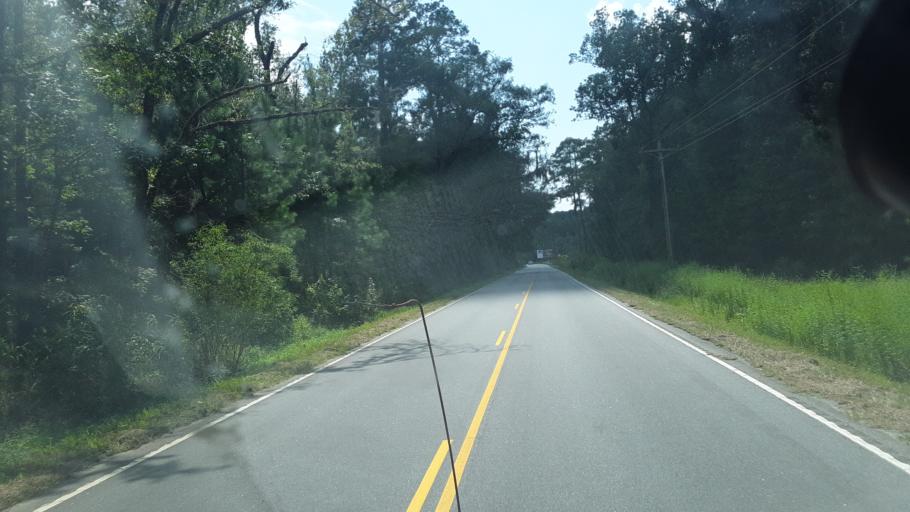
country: US
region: South Carolina
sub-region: Jasper County
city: Ridgeland
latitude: 32.4647
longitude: -80.8919
